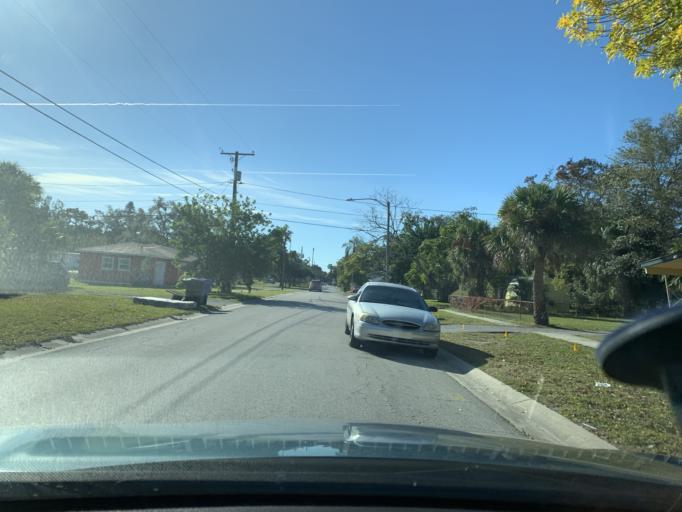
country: US
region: Florida
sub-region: Pinellas County
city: Gulfport
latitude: 27.7555
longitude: -82.6931
